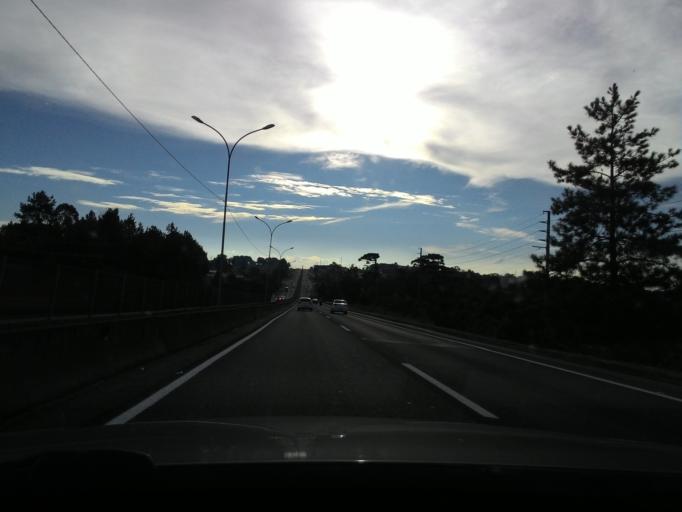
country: BR
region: Parana
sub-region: Quatro Barras
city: Quatro Barras
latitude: -25.3702
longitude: -49.1210
